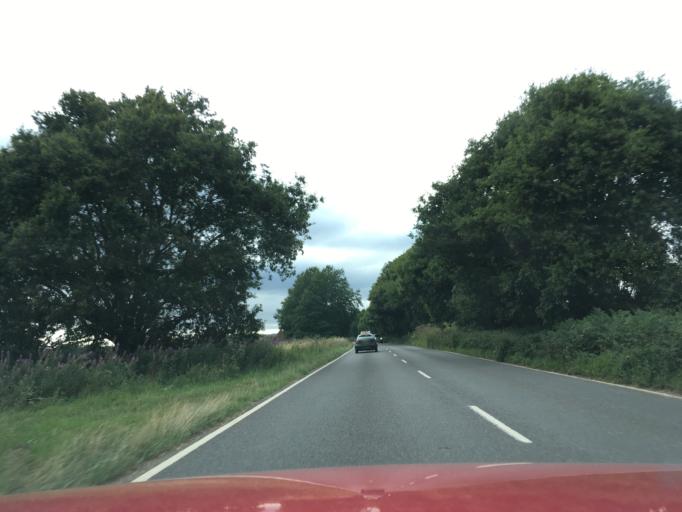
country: GB
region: England
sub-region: Hampshire
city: Liss
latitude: 51.0059
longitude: -0.8628
